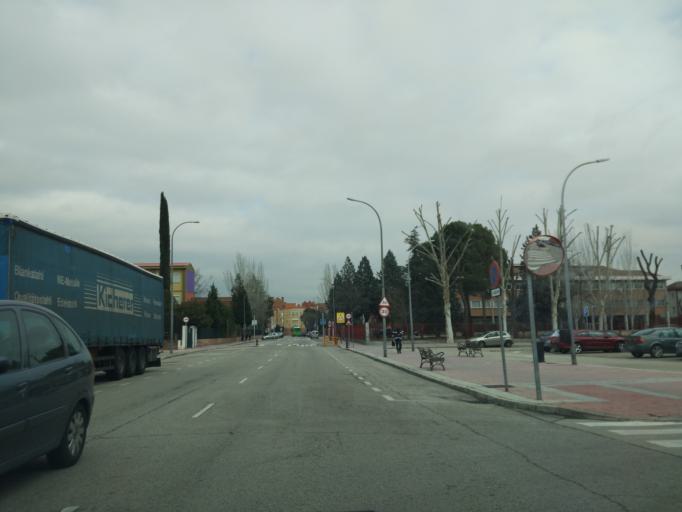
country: ES
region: Madrid
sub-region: Provincia de Madrid
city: Torrejon de Ardoz
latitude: 40.4614
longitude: -3.4888
